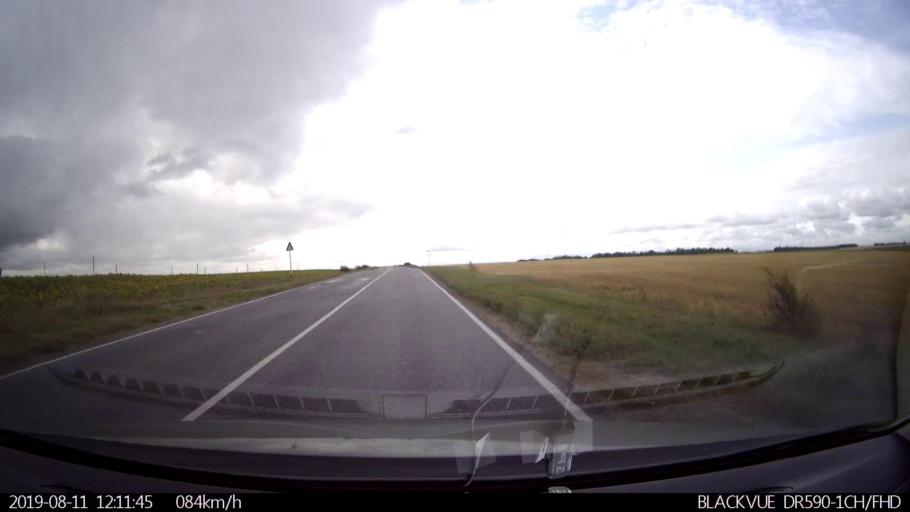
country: RU
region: Ulyanovsk
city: Silikatnyy
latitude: 53.9817
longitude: 48.0009
